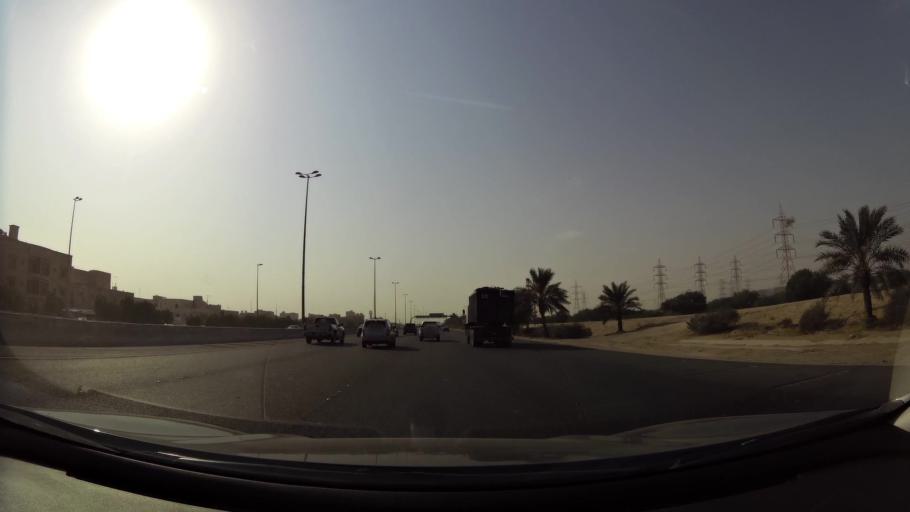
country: KW
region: Al Ahmadi
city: Al Ahmadi
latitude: 29.1039
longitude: 48.0961
